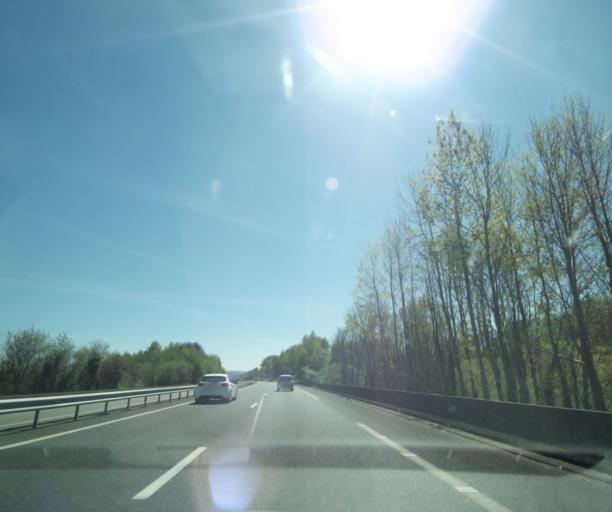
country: FR
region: Limousin
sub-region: Departement de la Correze
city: Uzerche
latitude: 45.4522
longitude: 1.5086
